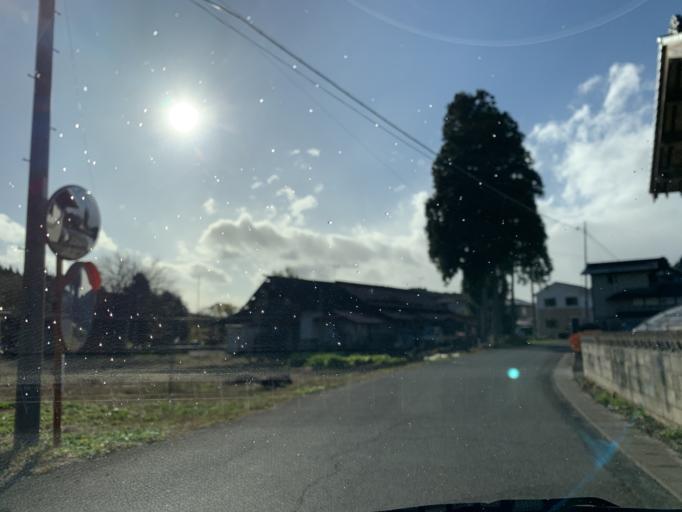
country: JP
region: Iwate
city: Ichinoseki
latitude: 39.0072
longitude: 141.0954
